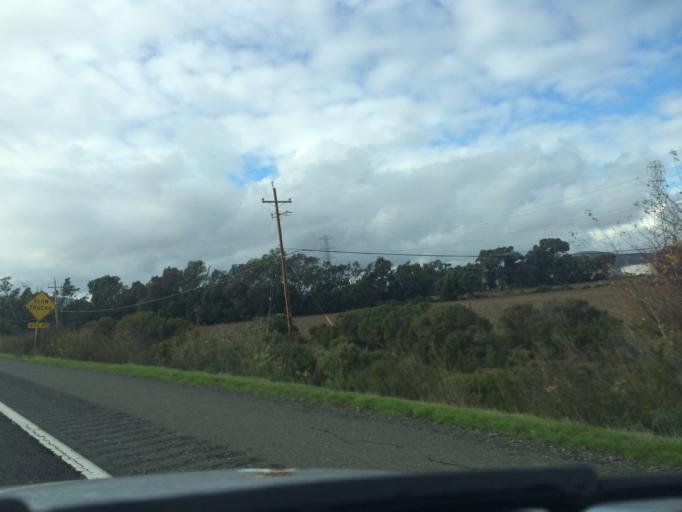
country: US
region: California
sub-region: Marin County
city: Black Point-Green Point
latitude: 38.1552
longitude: -122.4185
